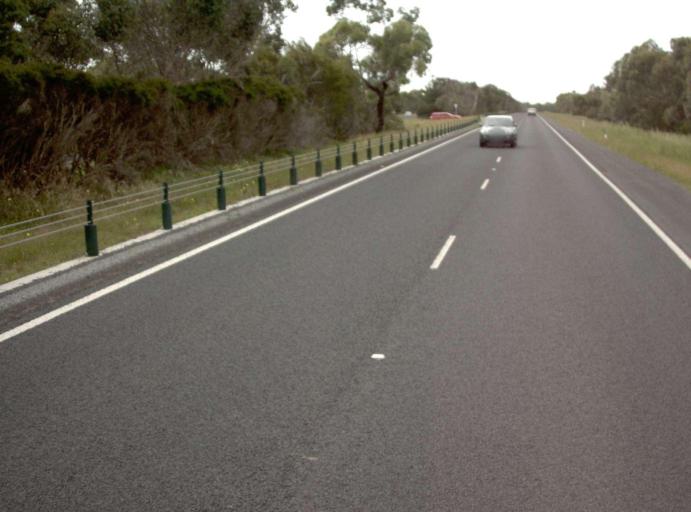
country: AU
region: Victoria
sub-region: Casey
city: Blind Bight
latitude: -38.1732
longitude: 145.3321
